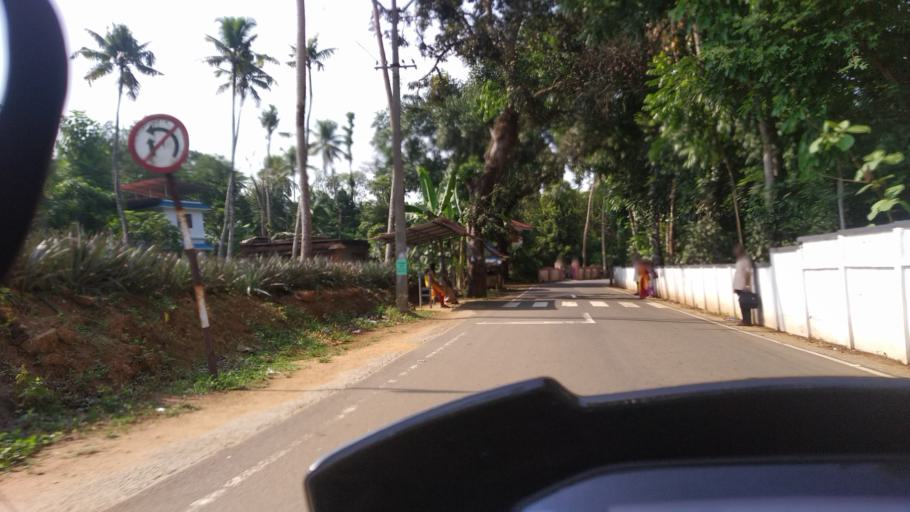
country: IN
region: Kerala
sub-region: Ernakulam
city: Piravam
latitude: 9.8457
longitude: 76.5348
